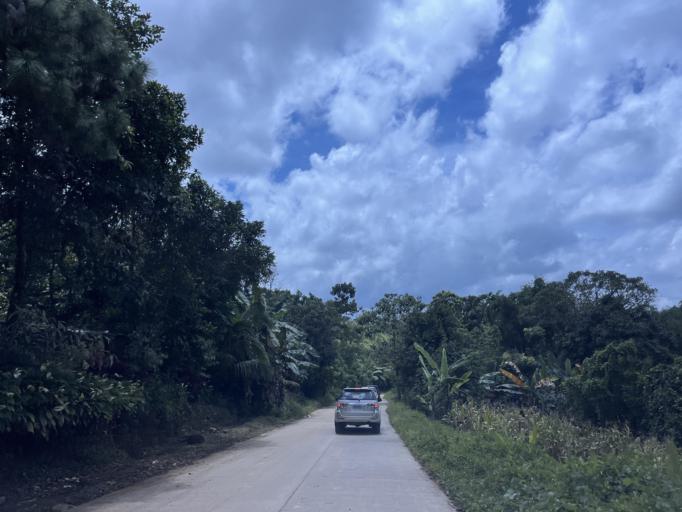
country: PH
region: Northern Mindanao
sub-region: Province of Bukidnon
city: Sumilao
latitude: 8.2839
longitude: 124.9446
